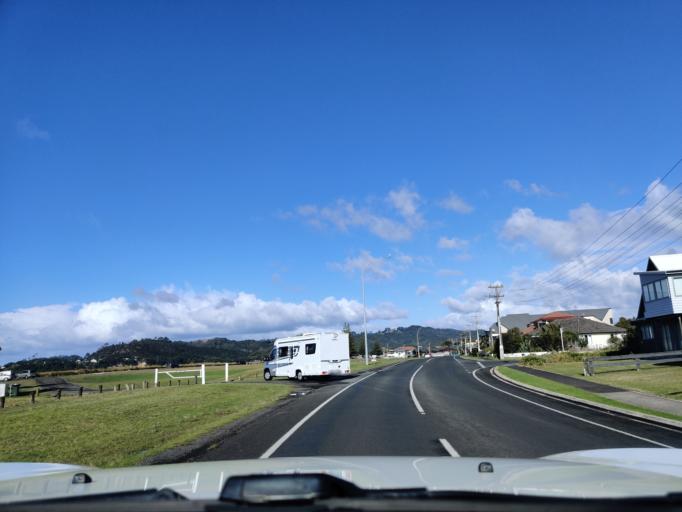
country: NZ
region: Waikato
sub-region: Thames-Coromandel District
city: Whitianga
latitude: -36.8208
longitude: 175.7001
